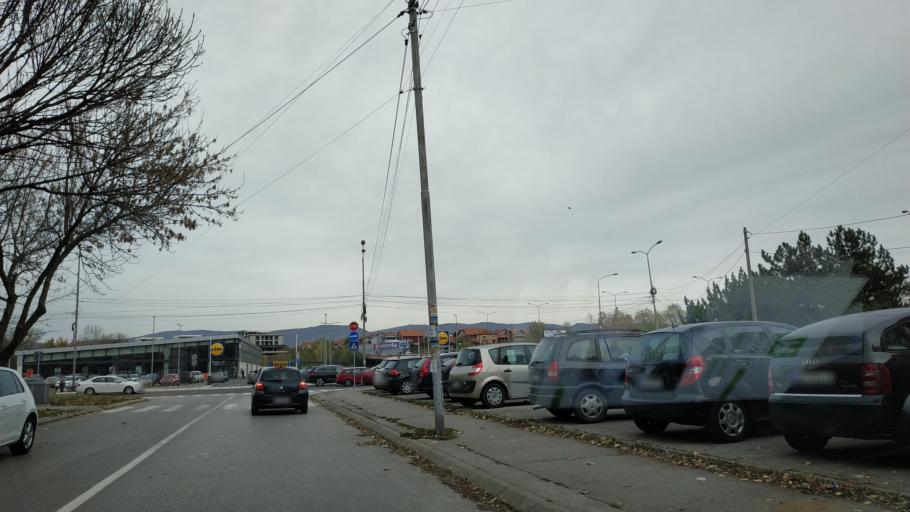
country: RS
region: Central Serbia
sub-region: Nisavski Okrug
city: Nis
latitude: 43.3205
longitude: 21.9359
